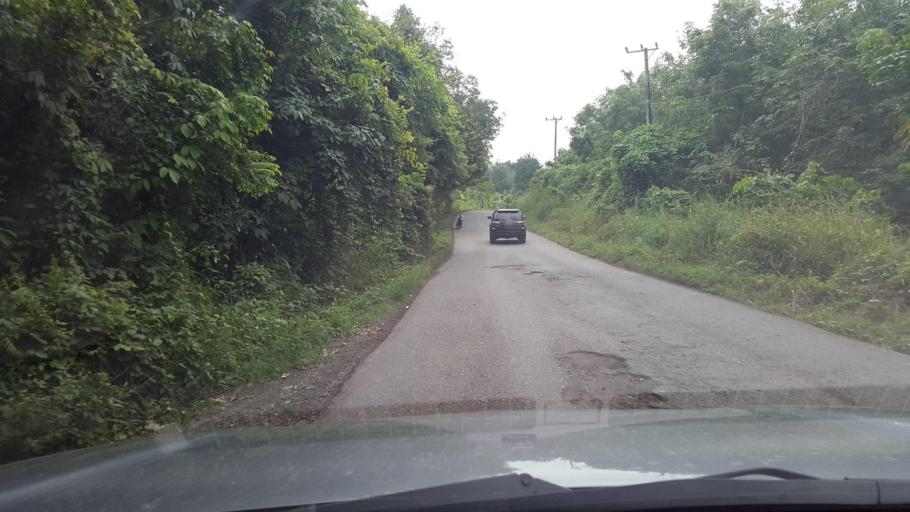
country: ID
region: South Sumatra
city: Gunungmenang
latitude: -3.3096
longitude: 104.0266
